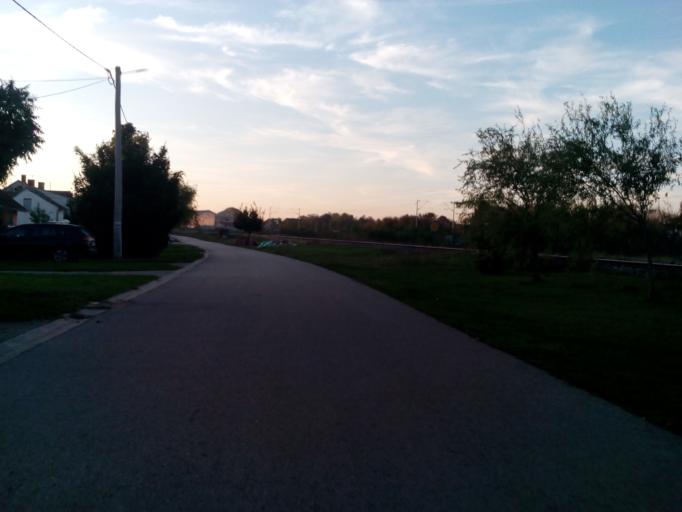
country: HR
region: Vukovarsko-Srijemska
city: Vinkovci
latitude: 45.2993
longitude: 18.8180
